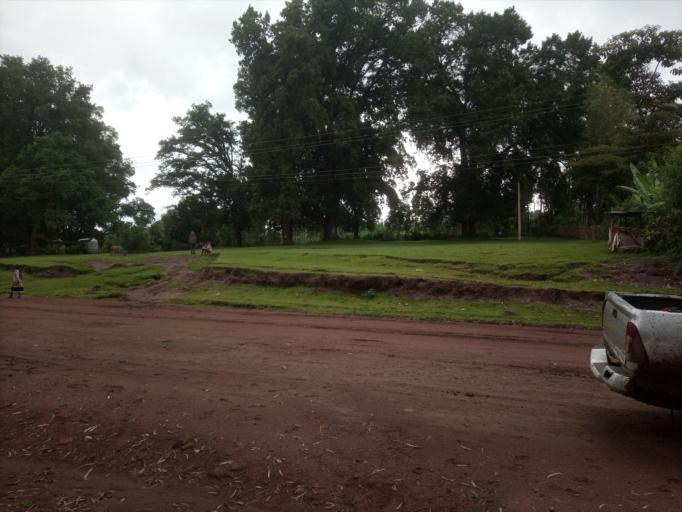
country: ET
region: Southern Nations, Nationalities, and People's Region
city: K'olito
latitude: 7.3431
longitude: 37.9195
